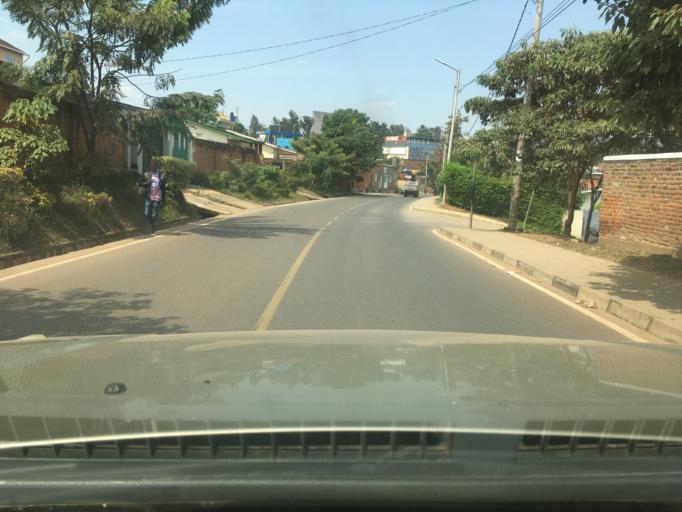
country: RW
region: Kigali
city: Kigali
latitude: -1.9654
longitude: 30.1015
